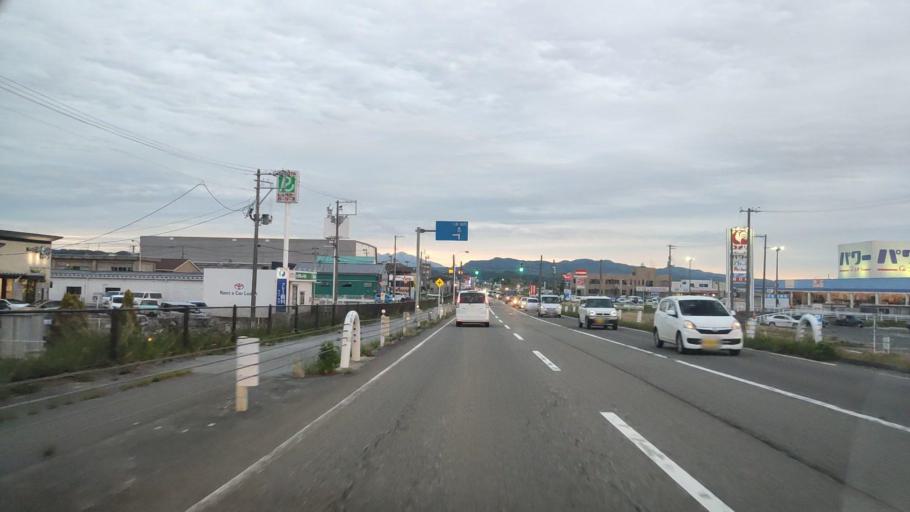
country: JP
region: Niigata
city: Niitsu-honcho
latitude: 37.7908
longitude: 139.1112
